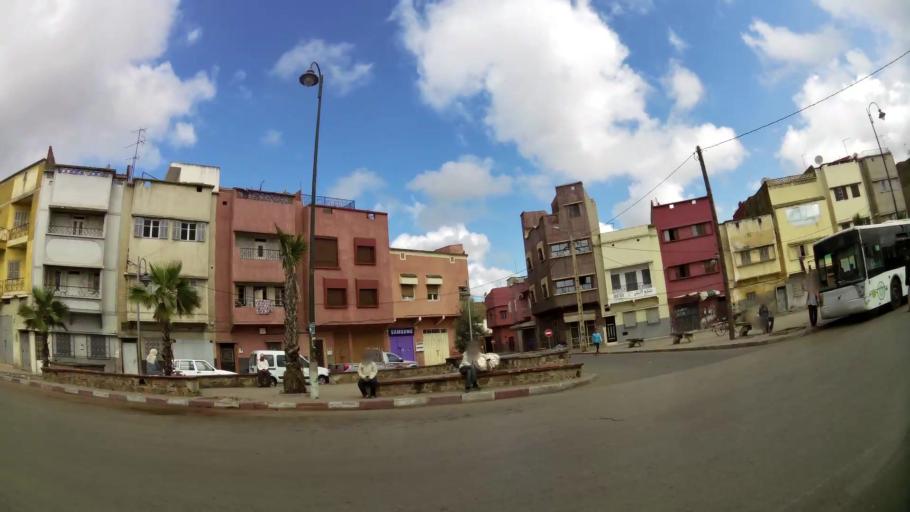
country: MA
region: Gharb-Chrarda-Beni Hssen
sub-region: Kenitra Province
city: Kenitra
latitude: 34.2614
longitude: -6.5631
